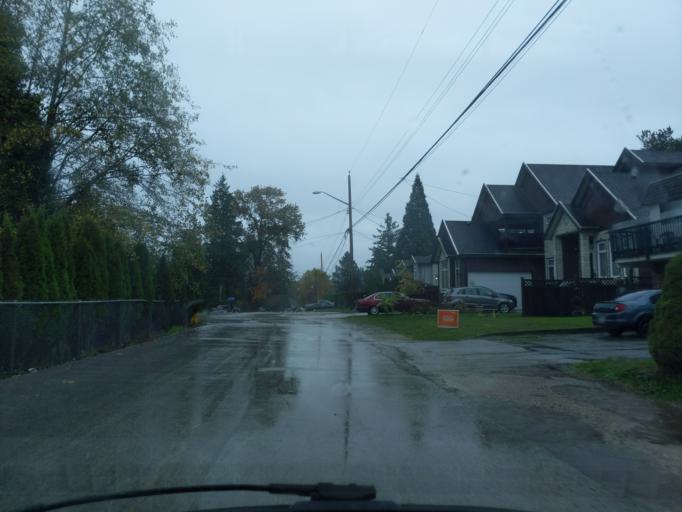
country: CA
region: British Columbia
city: New Westminster
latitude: 49.1980
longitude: -122.8603
